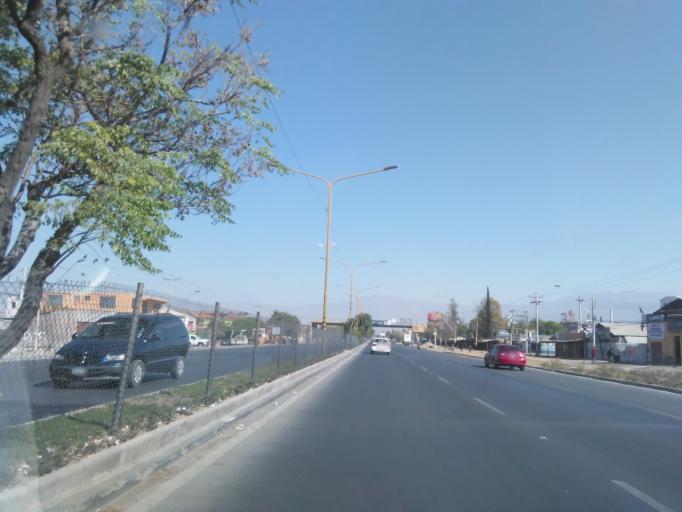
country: BO
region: Cochabamba
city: Cochabamba
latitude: -17.3912
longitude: -66.2517
